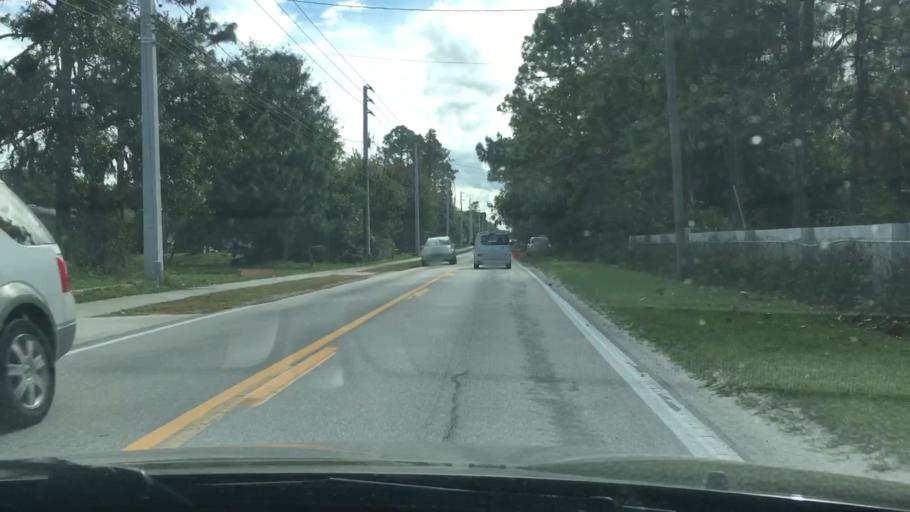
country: US
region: Florida
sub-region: Volusia County
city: Ormond Beach
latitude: 29.2718
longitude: -81.1294
